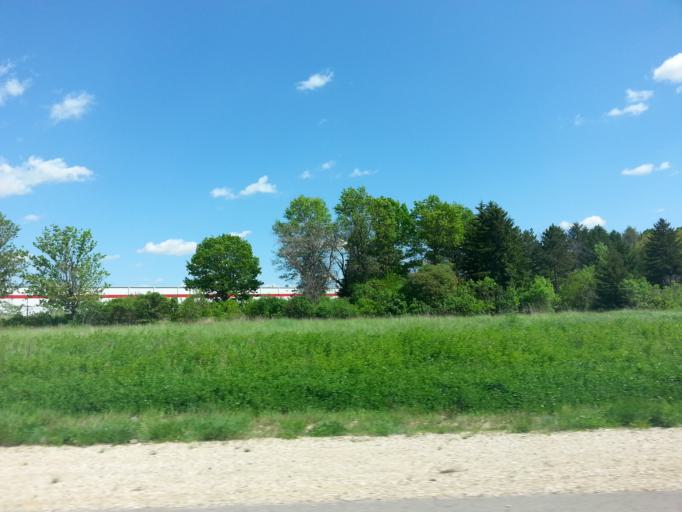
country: US
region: Wisconsin
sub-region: Rock County
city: Beloit
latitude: 42.5088
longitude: -88.9834
